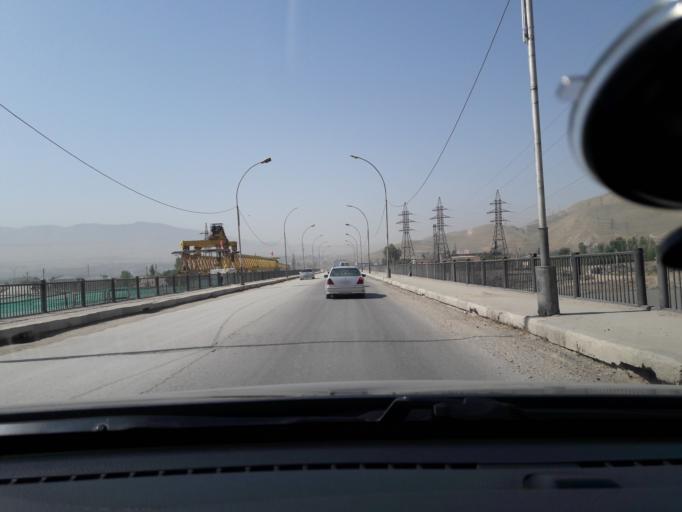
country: TJ
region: Dushanbe
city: Boshkengash
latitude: 38.4587
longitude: 68.7365
